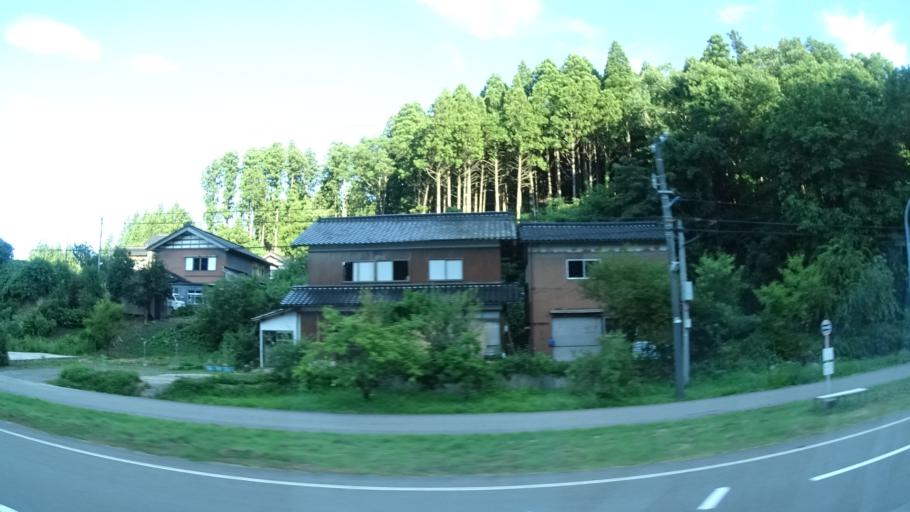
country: JP
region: Ishikawa
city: Nanao
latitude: 37.2930
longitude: 136.8935
